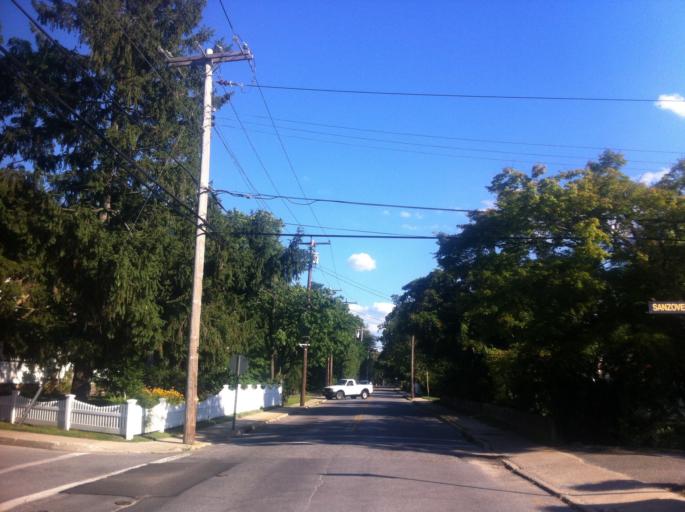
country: US
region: New York
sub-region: Nassau County
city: Bayville
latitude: 40.9068
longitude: -73.5724
